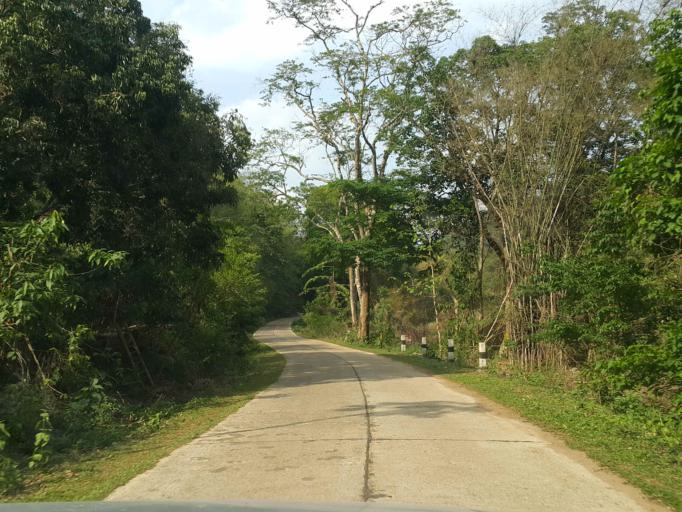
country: TH
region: Chiang Mai
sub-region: Amphoe Chiang Dao
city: Chiang Dao
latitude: 19.4028
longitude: 98.7825
